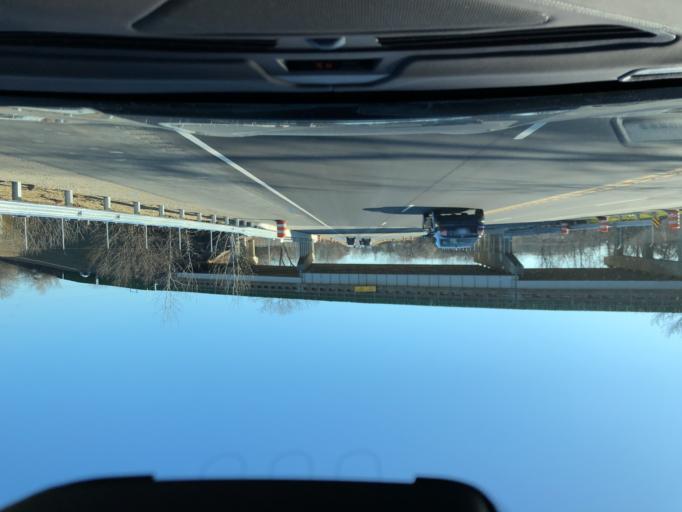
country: US
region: Michigan
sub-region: Washtenaw County
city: Ypsilanti
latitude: 42.2478
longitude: -83.5516
